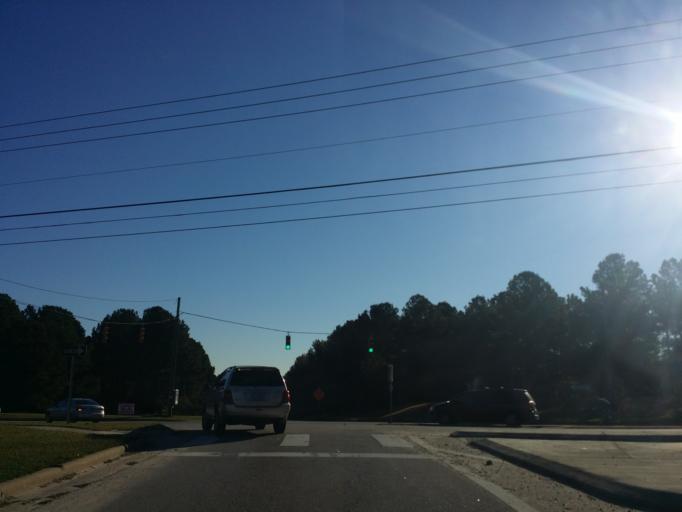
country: US
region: North Carolina
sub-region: Wake County
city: West Raleigh
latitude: 35.7560
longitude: -78.6663
